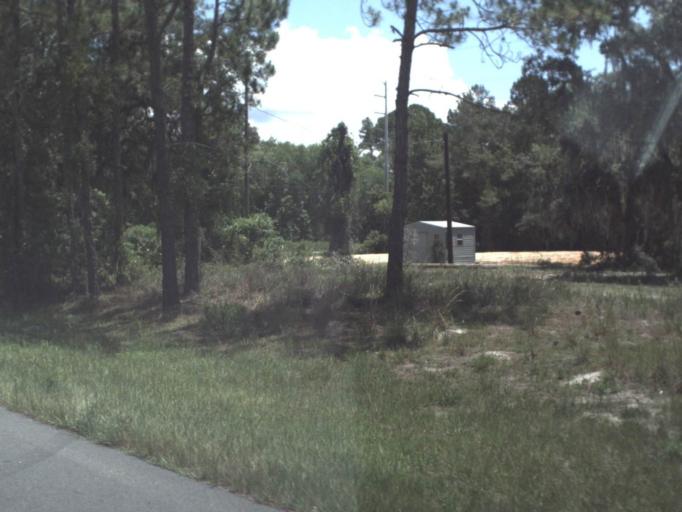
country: US
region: Florida
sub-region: Putnam County
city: Crescent City
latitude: 29.3786
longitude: -81.5089
